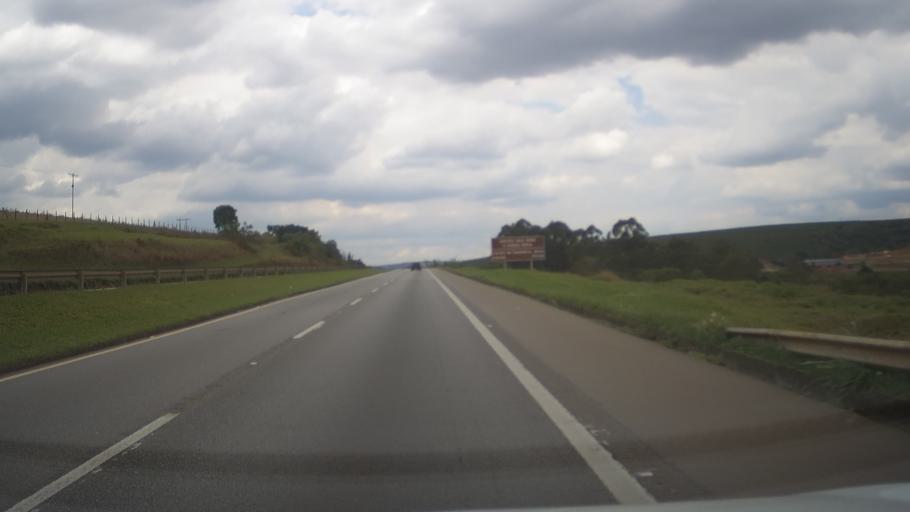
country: BR
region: Minas Gerais
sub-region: Tres Coracoes
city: Tres Coracoes
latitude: -21.5145
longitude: -45.2193
